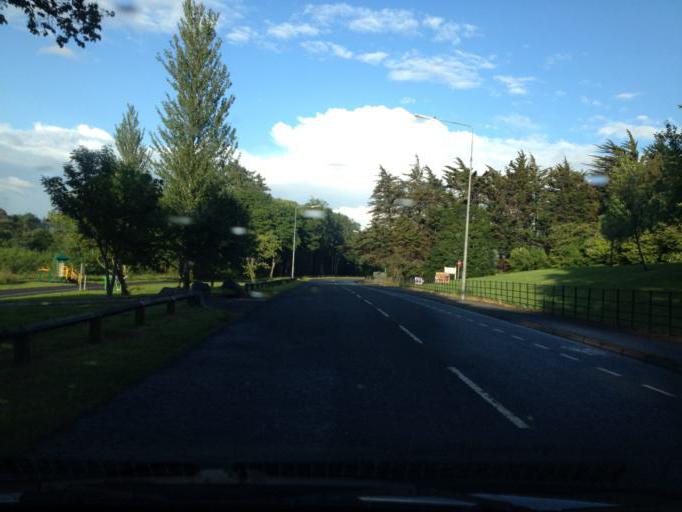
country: IE
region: Connaught
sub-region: Sligo
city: Sligo
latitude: 54.2654
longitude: -8.4504
